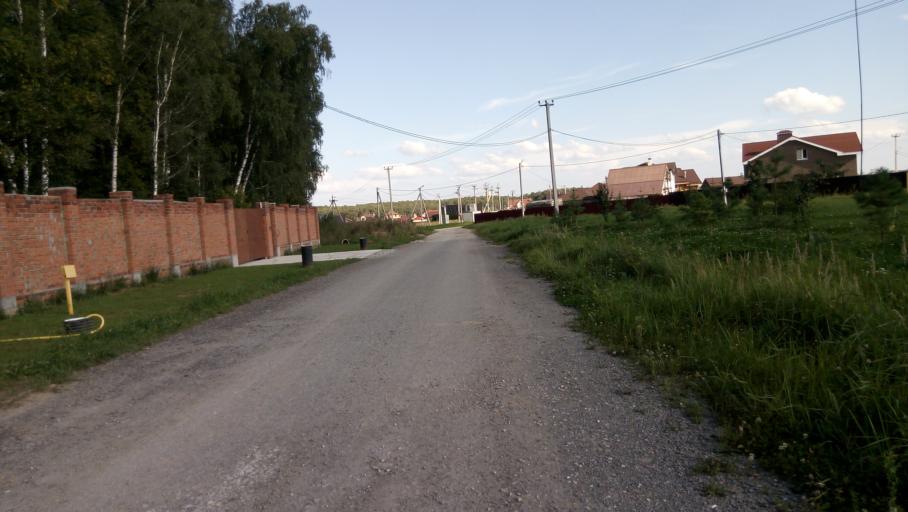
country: RU
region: Moskovskaya
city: Proletarskiy
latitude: 55.0477
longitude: 37.4088
